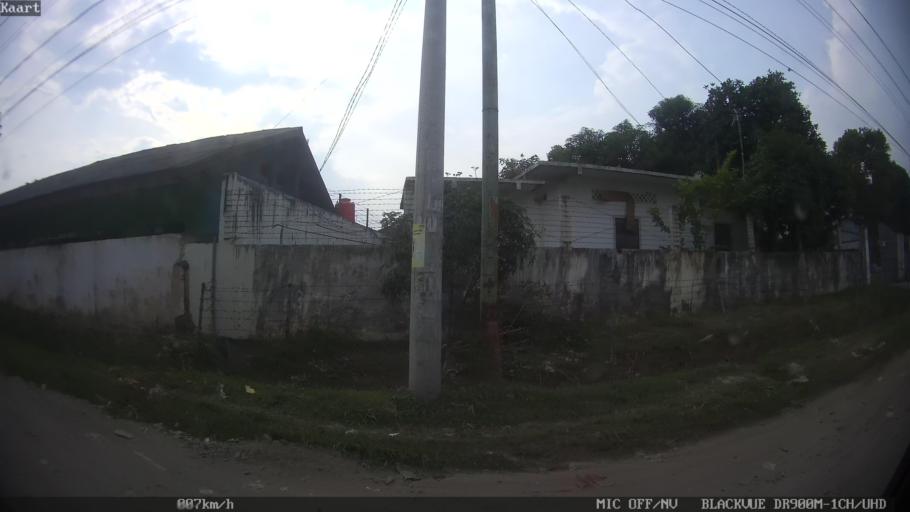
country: ID
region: Lampung
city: Panjang
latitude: -5.4506
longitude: 105.3086
